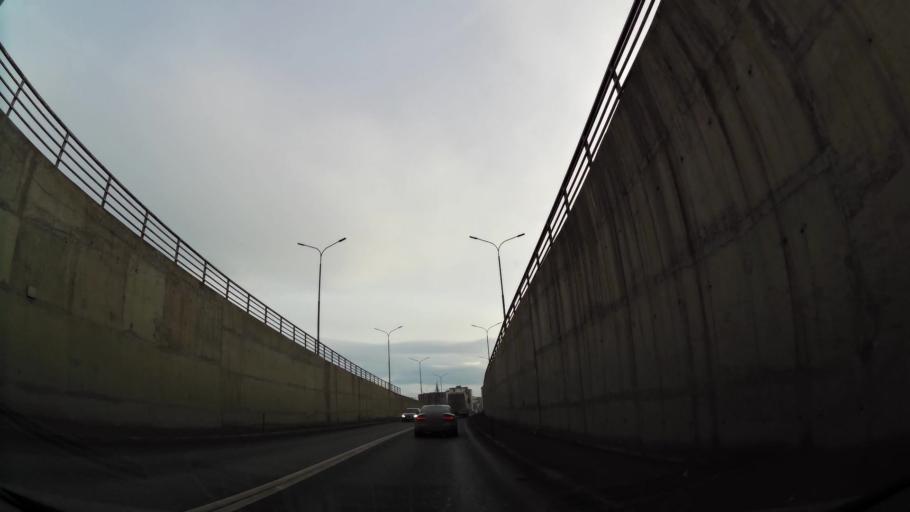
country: XK
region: Pristina
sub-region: Komuna e Prishtines
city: Pristina
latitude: 42.6453
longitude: 21.1561
